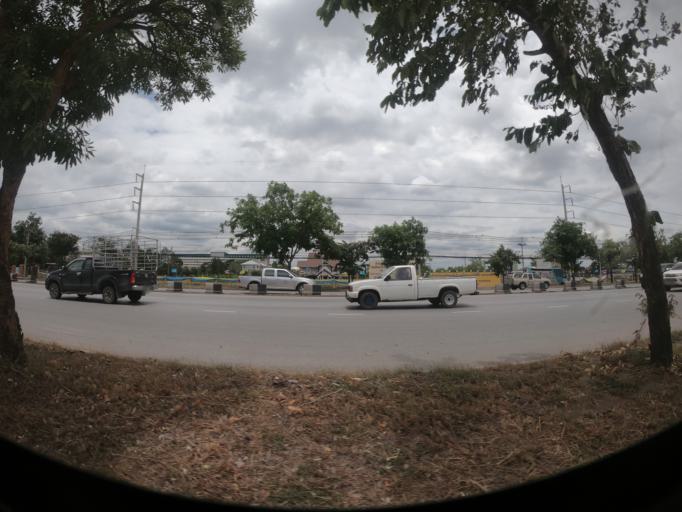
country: TH
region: Nakhon Ratchasima
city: Nakhon Ratchasima
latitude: 14.9544
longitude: 102.0305
